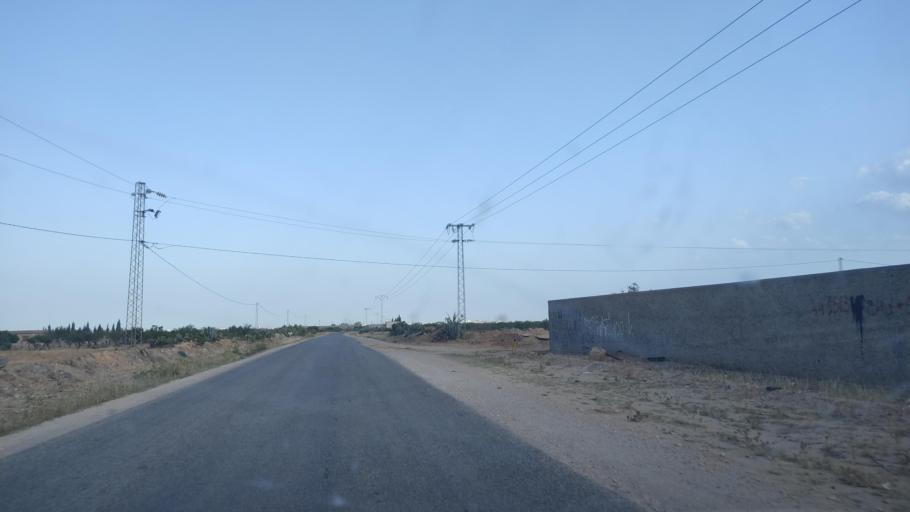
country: TN
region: Safaqis
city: Sfax
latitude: 34.8192
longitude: 10.6513
